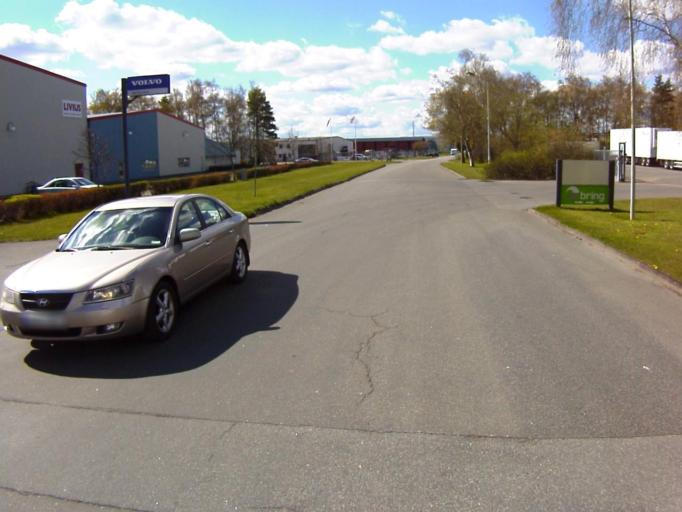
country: SE
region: Skane
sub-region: Kristianstads Kommun
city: Norra Asum
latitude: 56.0077
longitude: 14.1046
